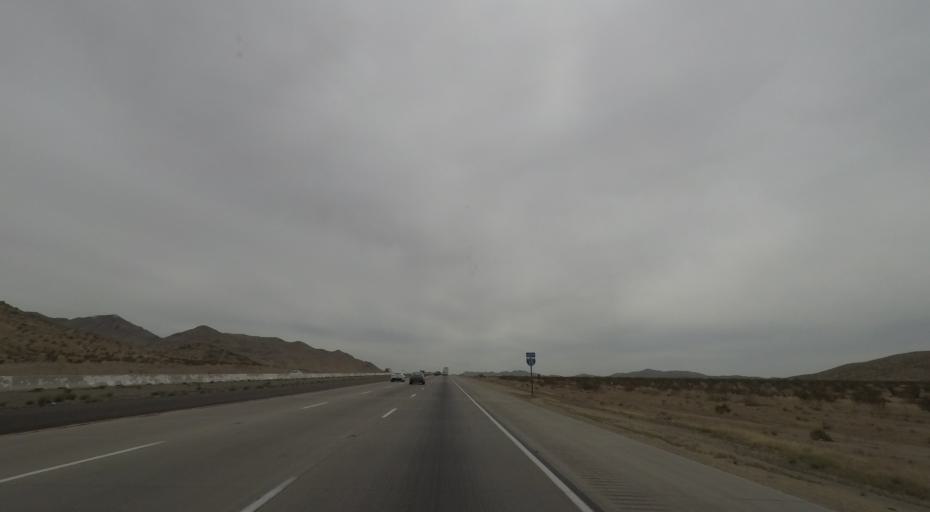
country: US
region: California
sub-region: San Bernardino County
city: Lenwood
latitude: 34.7453
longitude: -117.1739
